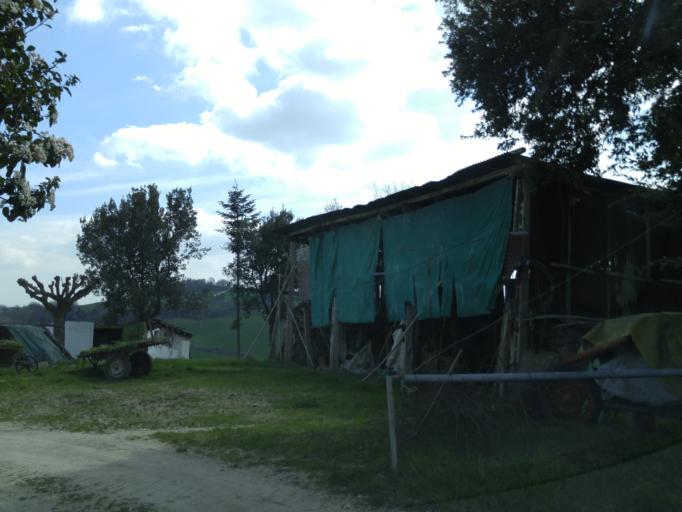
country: IT
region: The Marches
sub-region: Provincia di Pesaro e Urbino
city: Villanova
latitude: 43.7209
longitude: 12.9325
